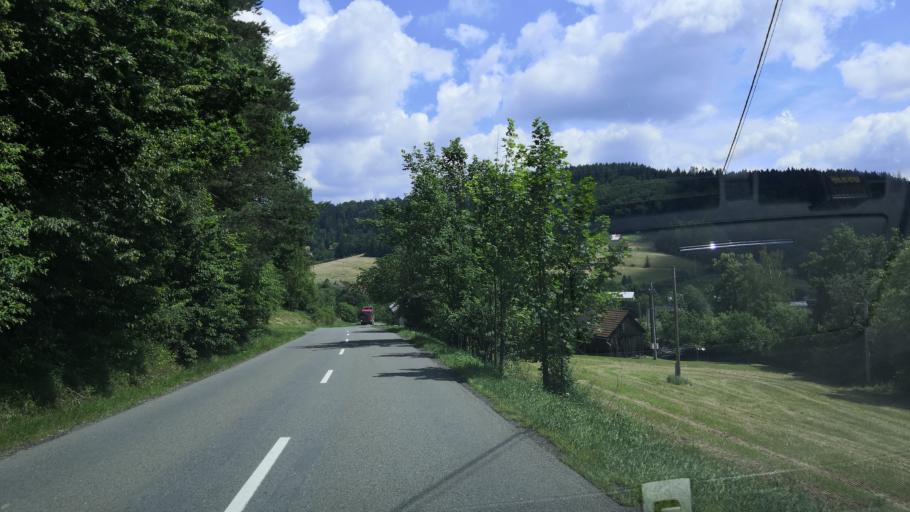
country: CZ
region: Zlin
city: Valasska Bystrice
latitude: 49.4258
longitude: 18.1173
